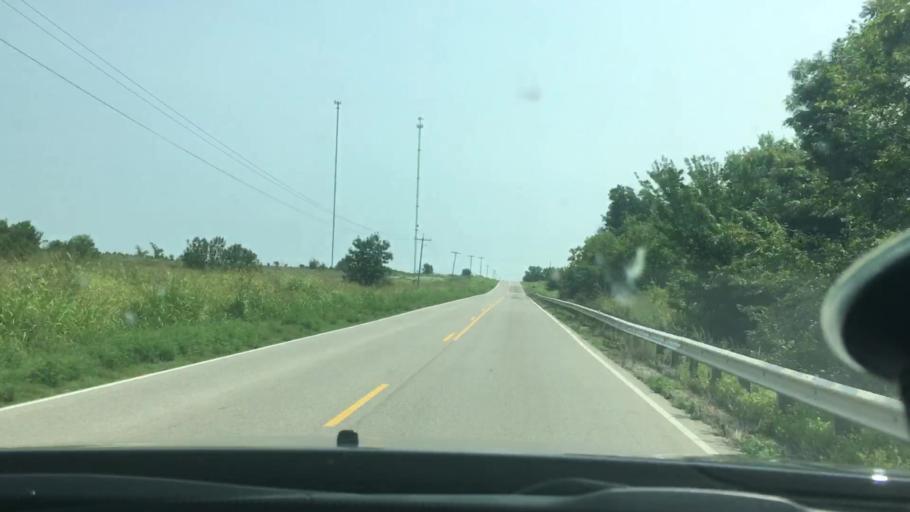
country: US
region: Oklahoma
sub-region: Garvin County
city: Stratford
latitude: 34.7967
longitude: -96.8911
